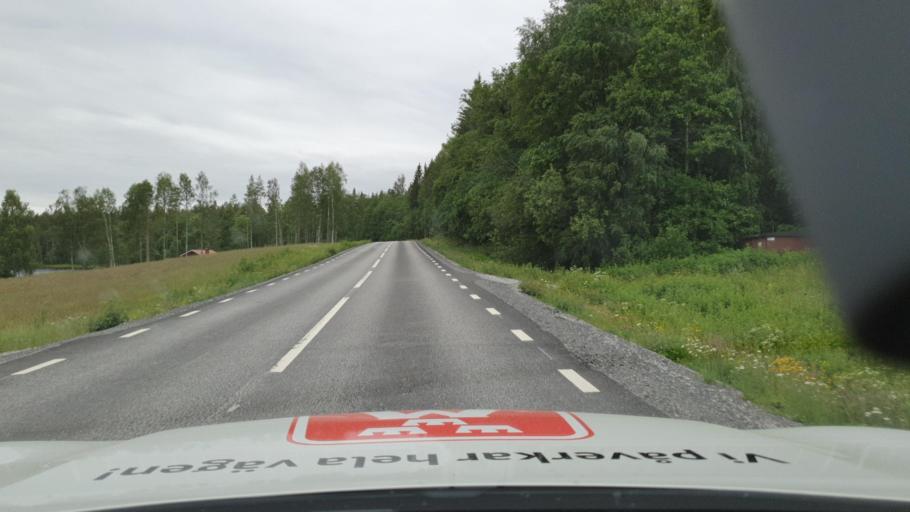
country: SE
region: Vaesterbotten
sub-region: Nordmalings Kommun
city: Nordmaling
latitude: 63.7149
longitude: 19.6344
